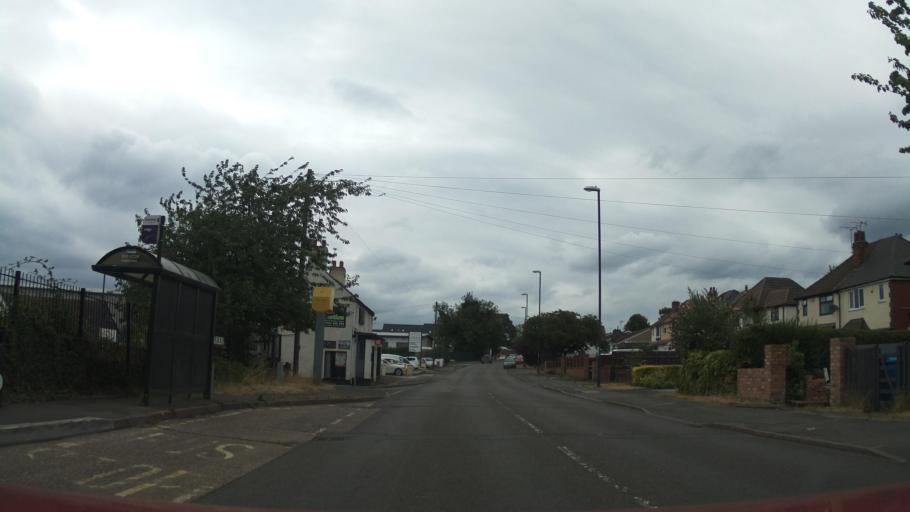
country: GB
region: England
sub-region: Derbyshire
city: Borrowash
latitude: 52.9120
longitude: -1.4015
